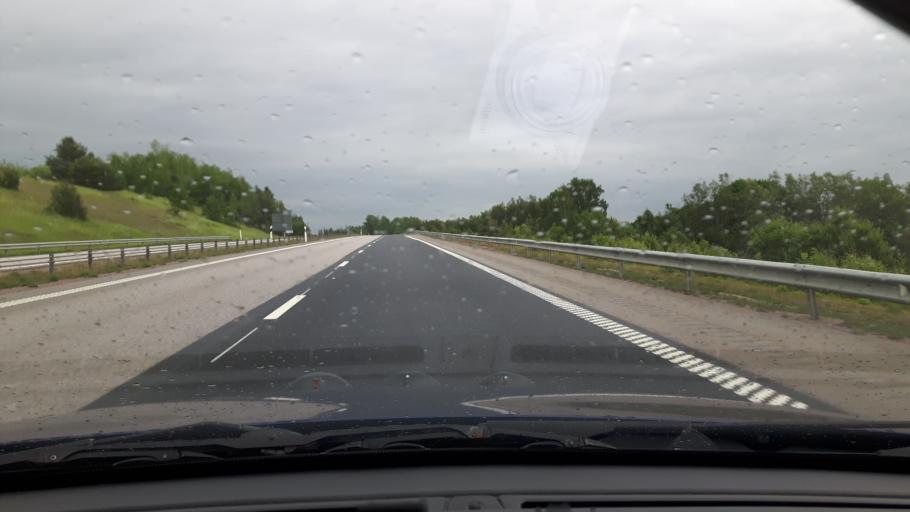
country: SE
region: OEstergoetland
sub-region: Mjolby Kommun
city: Mjolby
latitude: 58.3324
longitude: 15.1112
